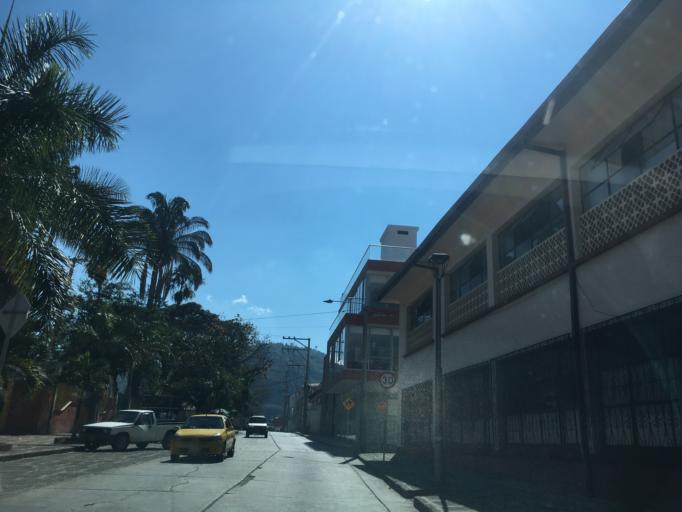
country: CO
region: Santander
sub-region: San Gil
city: San Gil
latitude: 6.5581
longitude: -73.1315
